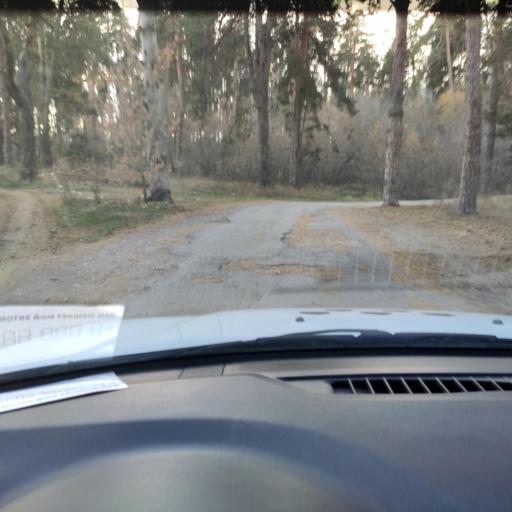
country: RU
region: Samara
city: Tol'yatti
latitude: 53.5067
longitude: 49.3885
